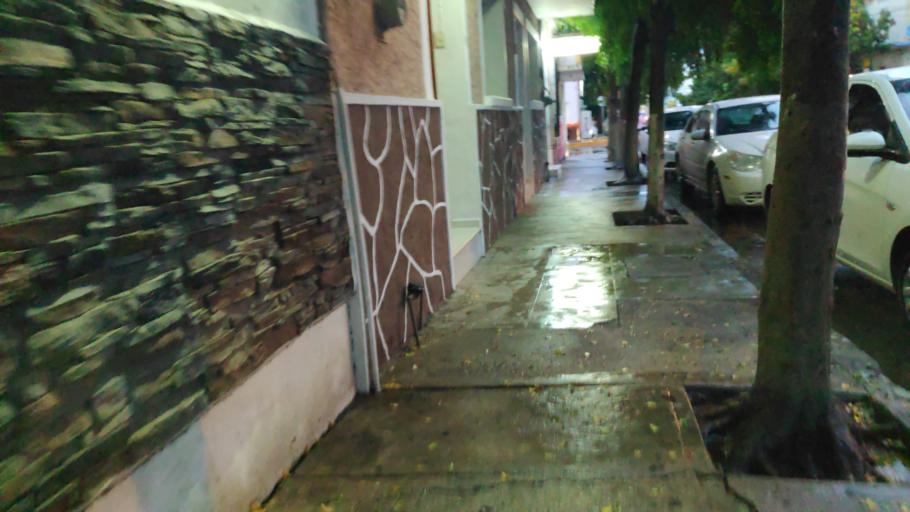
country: MX
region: Sinaloa
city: Culiacan
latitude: 24.8085
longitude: -107.4027
